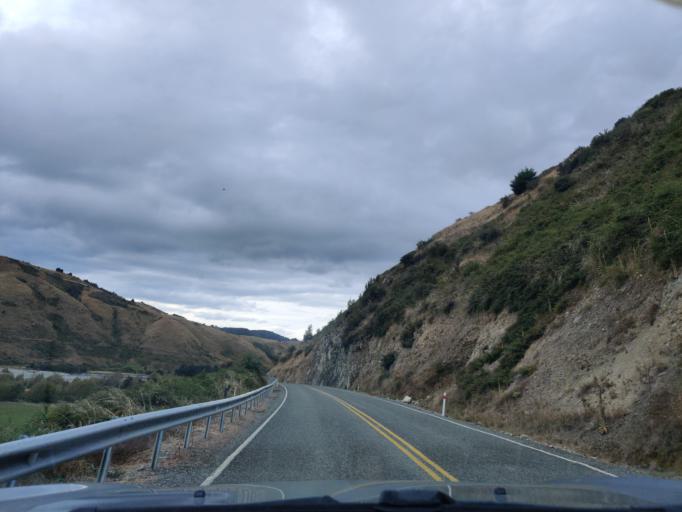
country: NZ
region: Tasman
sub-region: Tasman District
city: Wakefield
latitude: -41.7053
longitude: 172.6699
